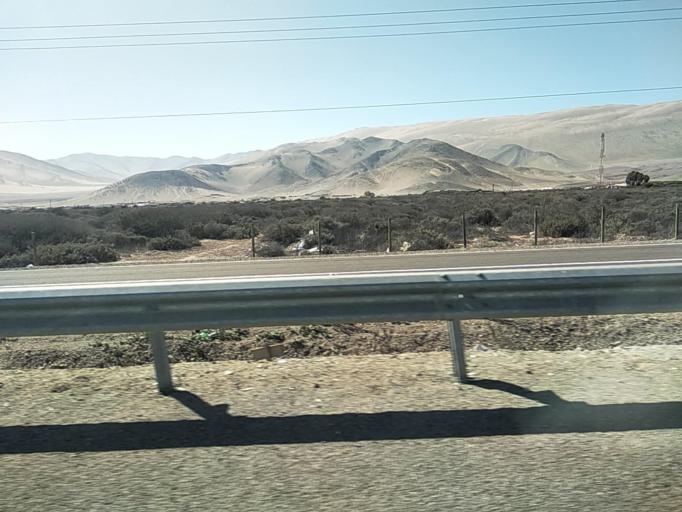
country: CL
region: Atacama
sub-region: Provincia de Copiapo
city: Copiapo
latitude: -27.2950
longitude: -70.4721
